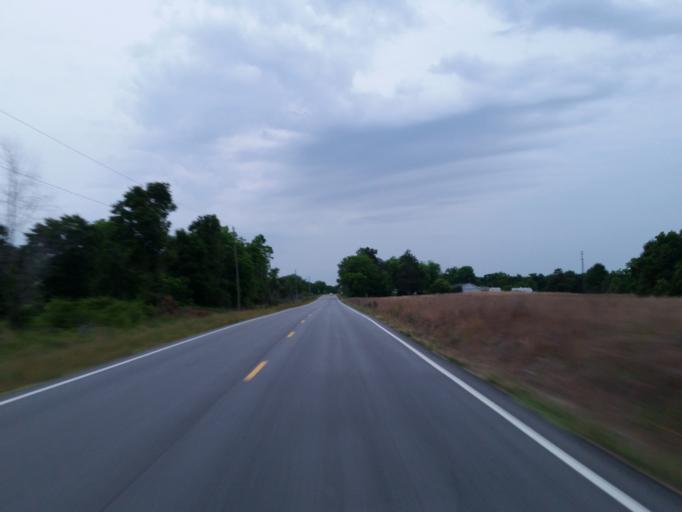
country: US
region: Georgia
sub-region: Turner County
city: Ashburn
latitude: 31.8086
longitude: -83.7170
